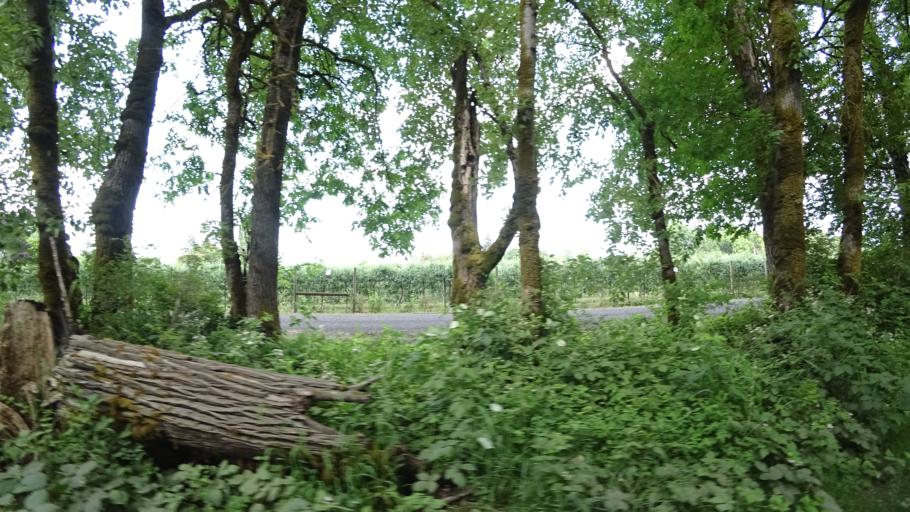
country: US
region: Oregon
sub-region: Washington County
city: Oak Hills
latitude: 45.6297
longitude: -122.7997
